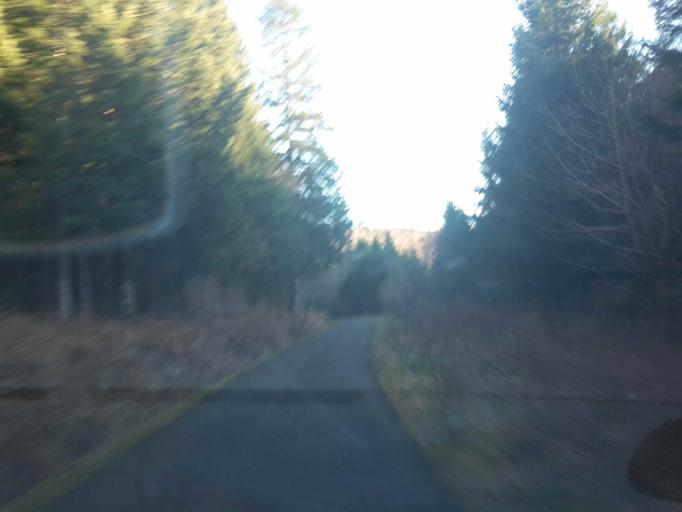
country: FR
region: Auvergne
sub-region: Departement du Cantal
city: Riom-es-Montagnes
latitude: 45.2204
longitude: 2.5763
